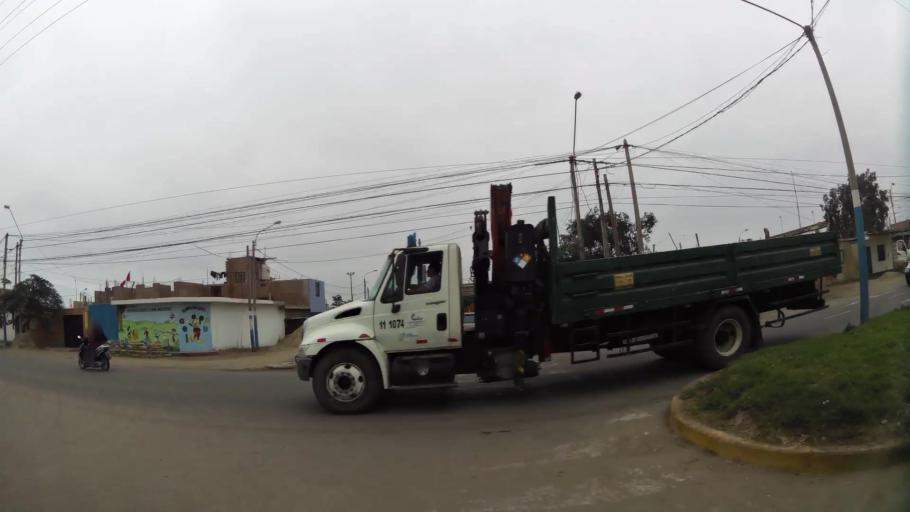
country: PE
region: Ica
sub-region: Provincia de Pisco
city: Pisco
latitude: -13.7179
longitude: -76.1957
